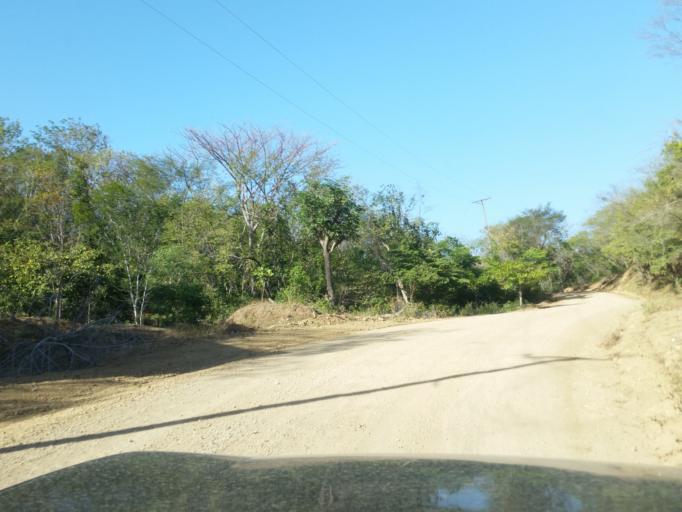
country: NI
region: Rivas
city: San Juan del Sur
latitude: 11.1679
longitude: -85.7973
